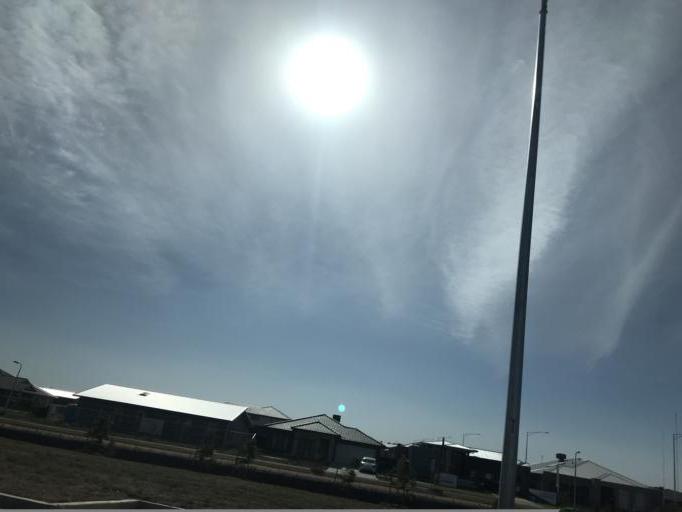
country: AU
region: Victoria
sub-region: Ballarat North
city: Newington
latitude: -37.5422
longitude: 143.7836
